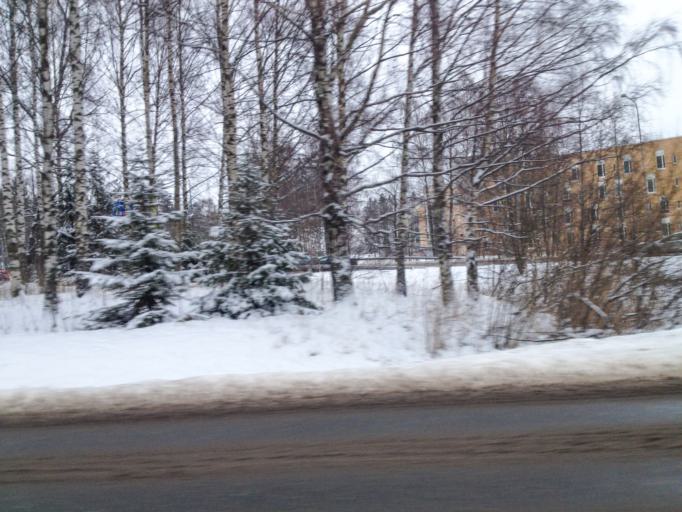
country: FI
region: Uusimaa
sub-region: Helsinki
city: Vantaa
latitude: 60.2226
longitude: 25.0805
